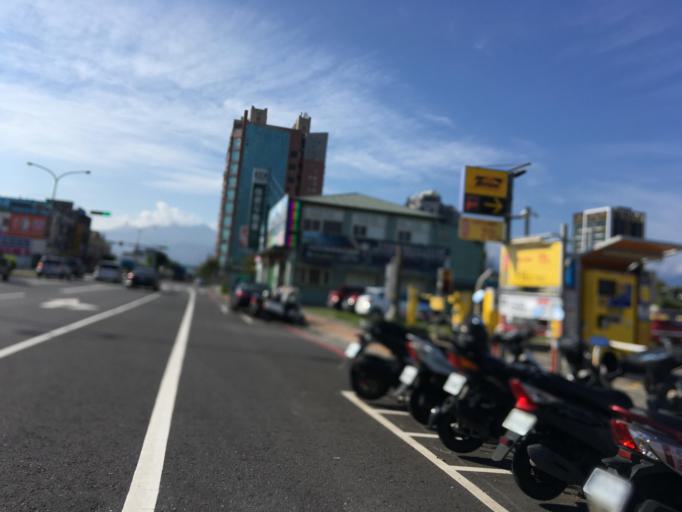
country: TW
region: Taiwan
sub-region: Yilan
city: Yilan
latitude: 24.6787
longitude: 121.7777
